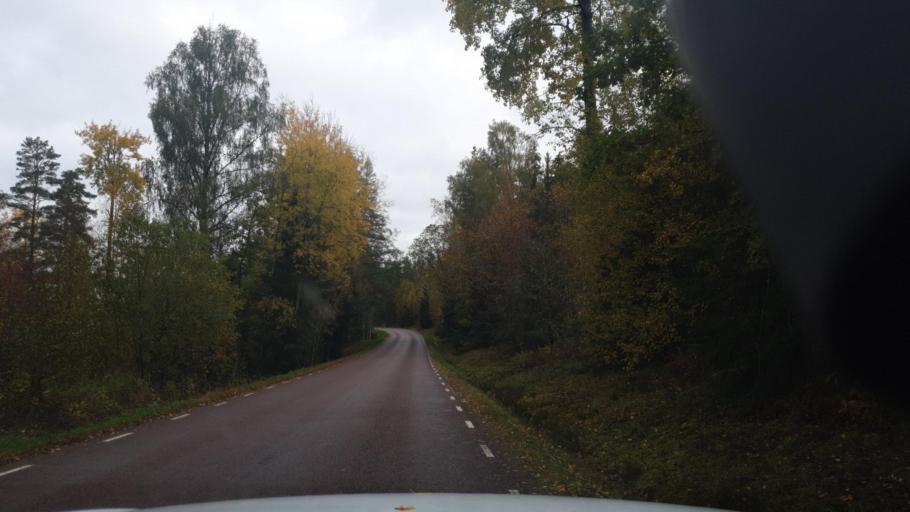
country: SE
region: Vaermland
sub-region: Grums Kommun
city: Grums
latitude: 59.4182
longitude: 13.0849
